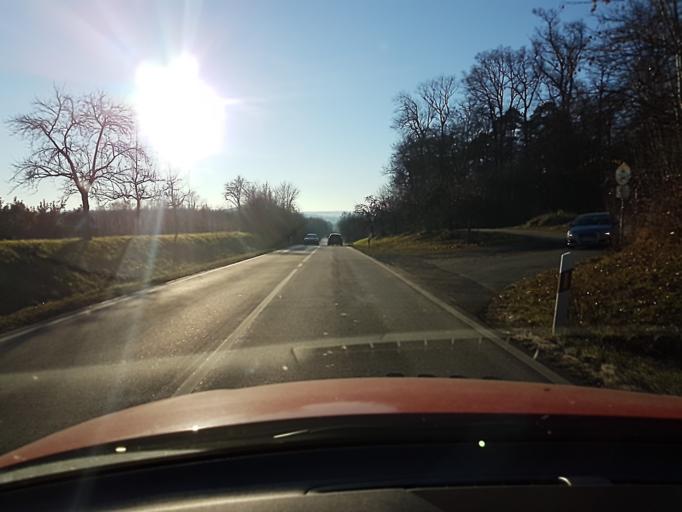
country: DE
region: Baden-Wuerttemberg
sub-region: Karlsruhe Region
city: Illingen
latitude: 48.9645
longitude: 8.9426
